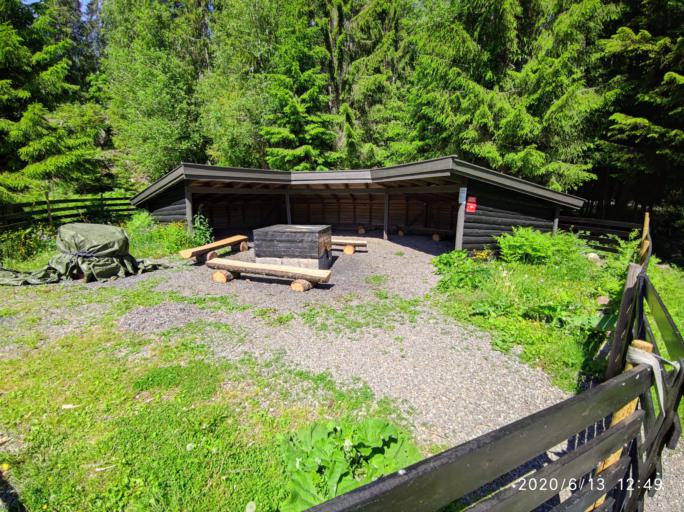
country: NO
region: Akershus
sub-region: Asker
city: Asker
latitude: 59.8649
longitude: 10.4067
